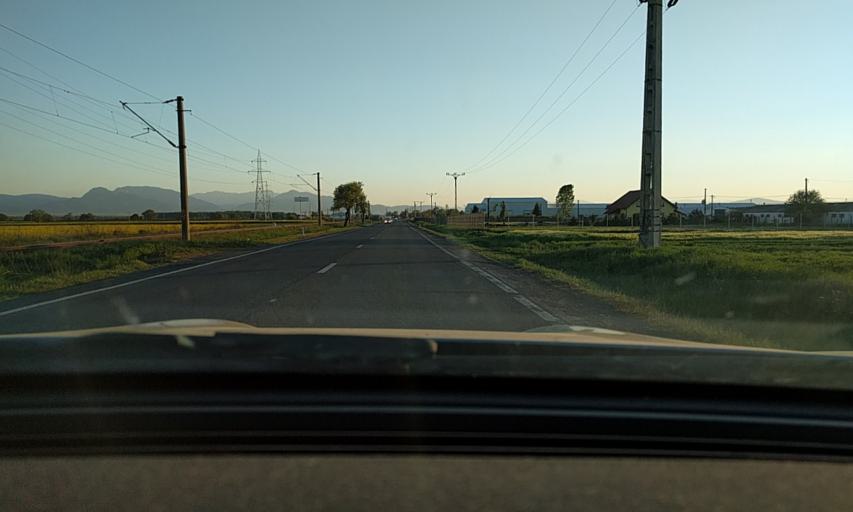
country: RO
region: Covasna
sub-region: Comuna Chichis
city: Chichis
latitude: 45.7703
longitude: 25.8032
